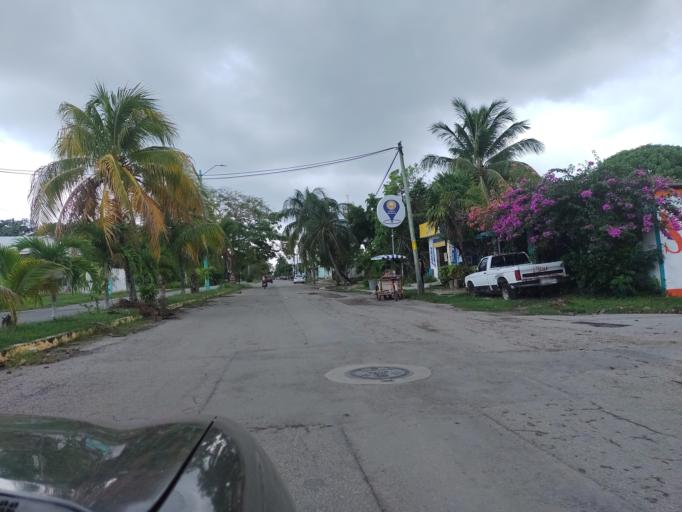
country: MX
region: Quintana Roo
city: Chetumal
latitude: 18.5184
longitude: -88.2769
